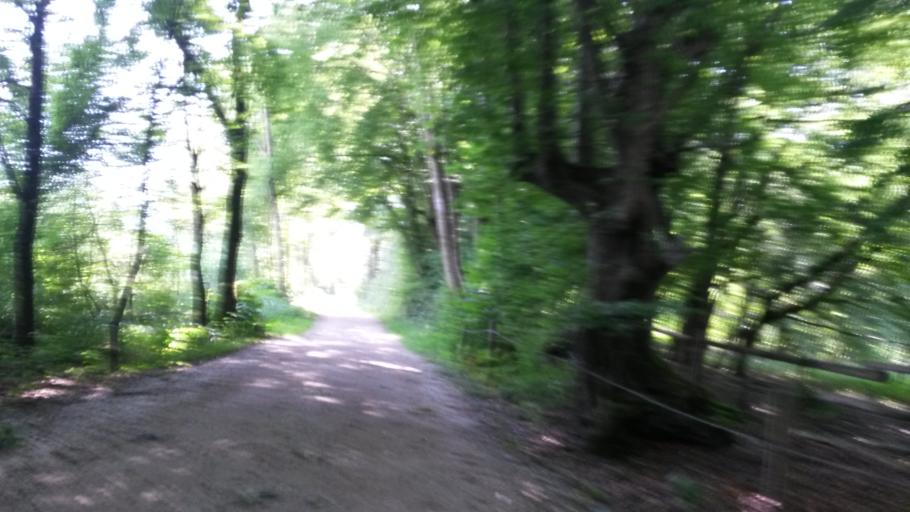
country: DE
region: Bavaria
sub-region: Upper Bavaria
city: Gstadt am Chiemsee
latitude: 47.8781
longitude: 12.4122
